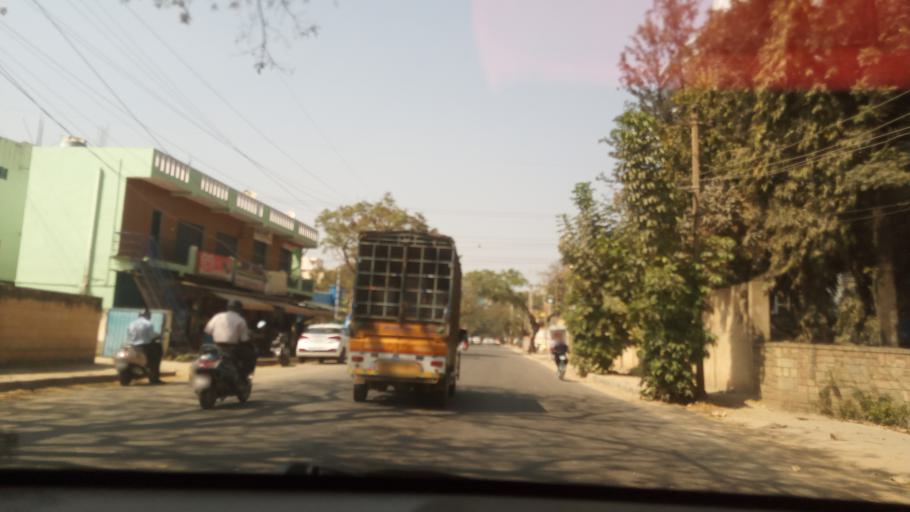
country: IN
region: Karnataka
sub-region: Bangalore Urban
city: Bangalore
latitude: 12.9897
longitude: 77.7068
